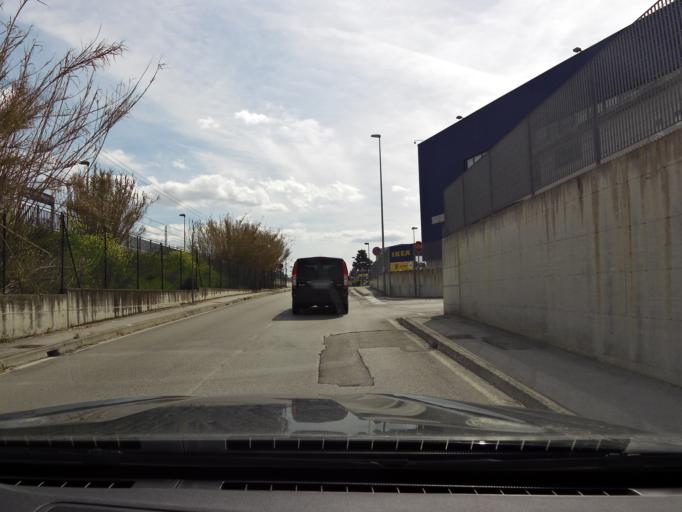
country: IT
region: The Marches
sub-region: Provincia di Ancona
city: San Biagio
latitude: 43.5306
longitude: 13.5202
